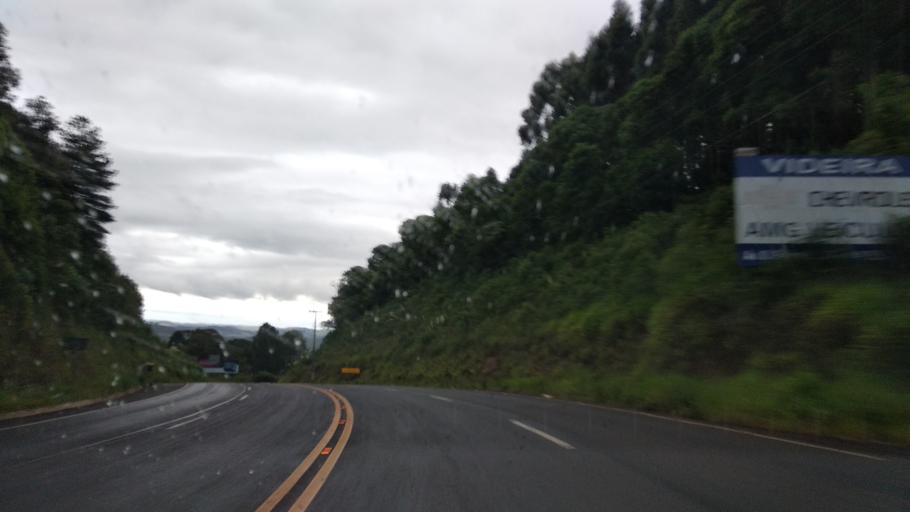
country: BR
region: Santa Catarina
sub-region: Videira
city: Videira
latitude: -27.0524
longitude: -51.1811
